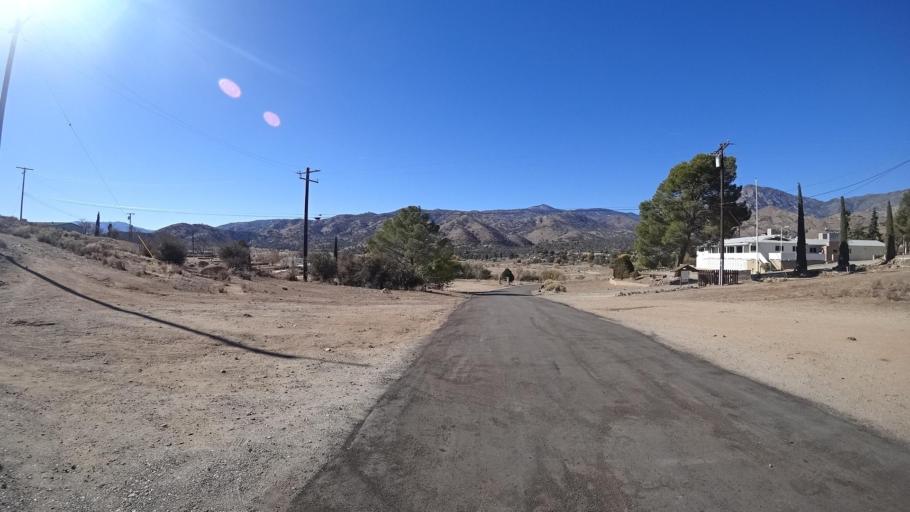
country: US
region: California
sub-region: Kern County
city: Wofford Heights
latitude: 35.7037
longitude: -118.4449
